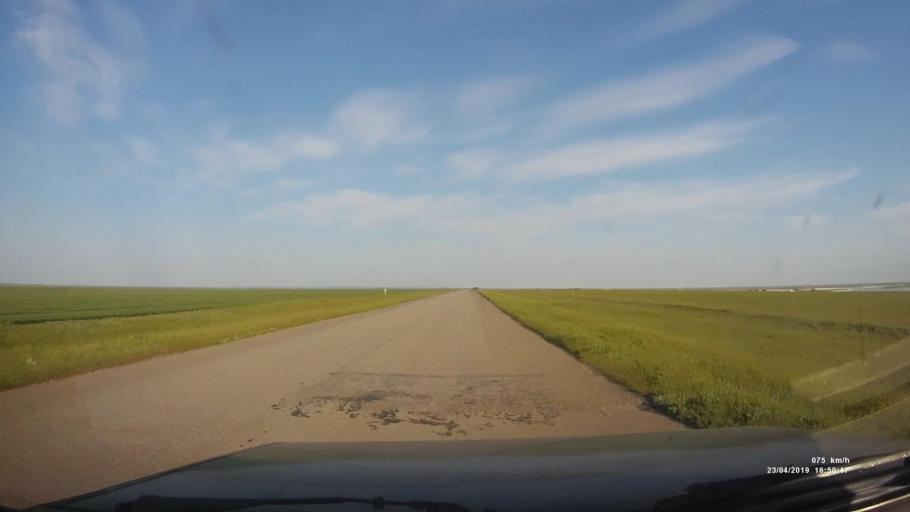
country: RU
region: Kalmykiya
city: Priyutnoye
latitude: 46.3256
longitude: 43.2967
